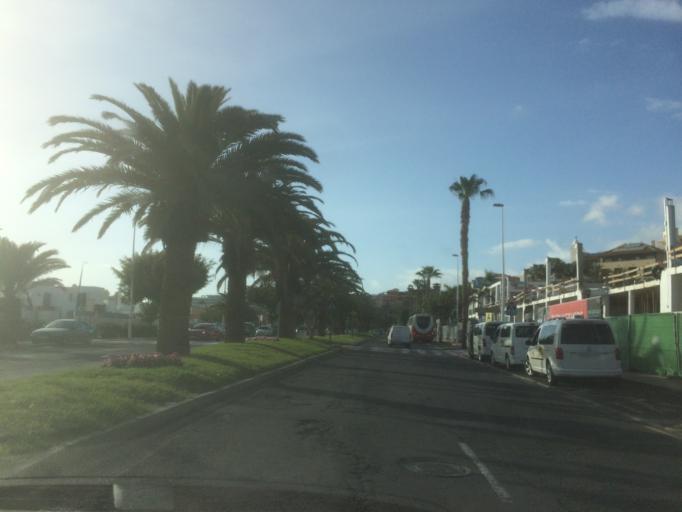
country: ES
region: Canary Islands
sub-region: Provincia de Santa Cruz de Tenerife
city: Playa de las Americas
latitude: 28.0915
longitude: -16.7355
